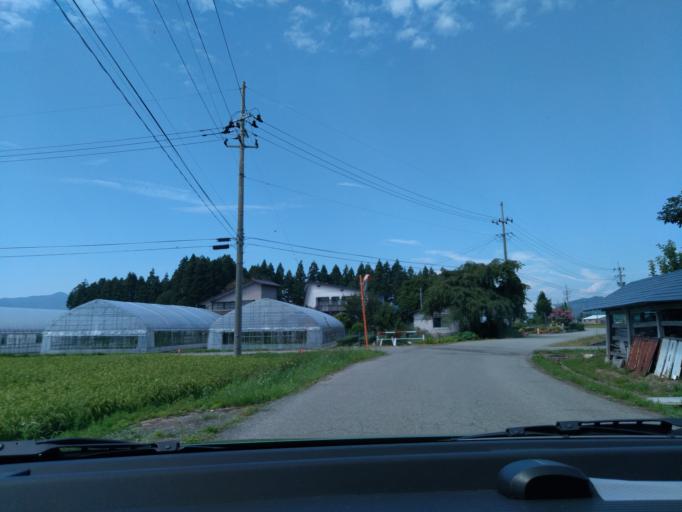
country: JP
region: Akita
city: Kakunodatemachi
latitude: 39.6107
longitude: 140.5943
